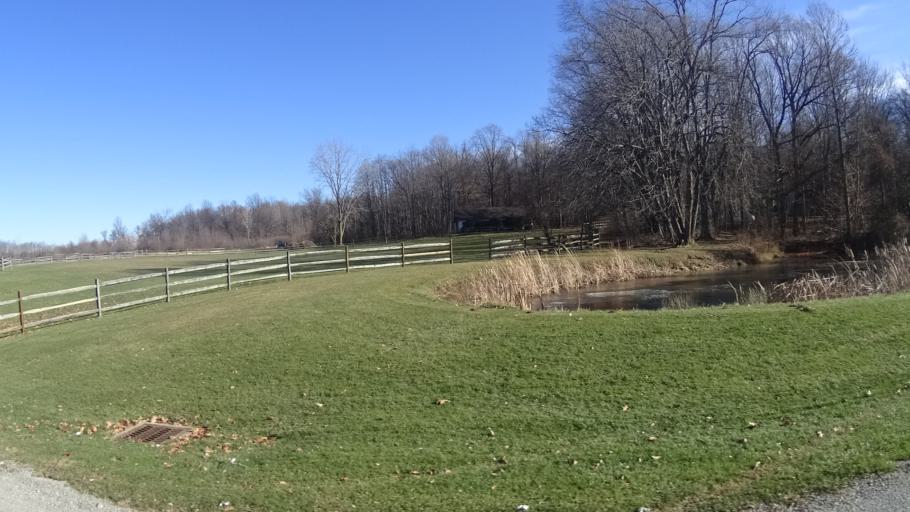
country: US
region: Ohio
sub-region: Lorain County
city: South Amherst
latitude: 41.3556
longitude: -82.2920
